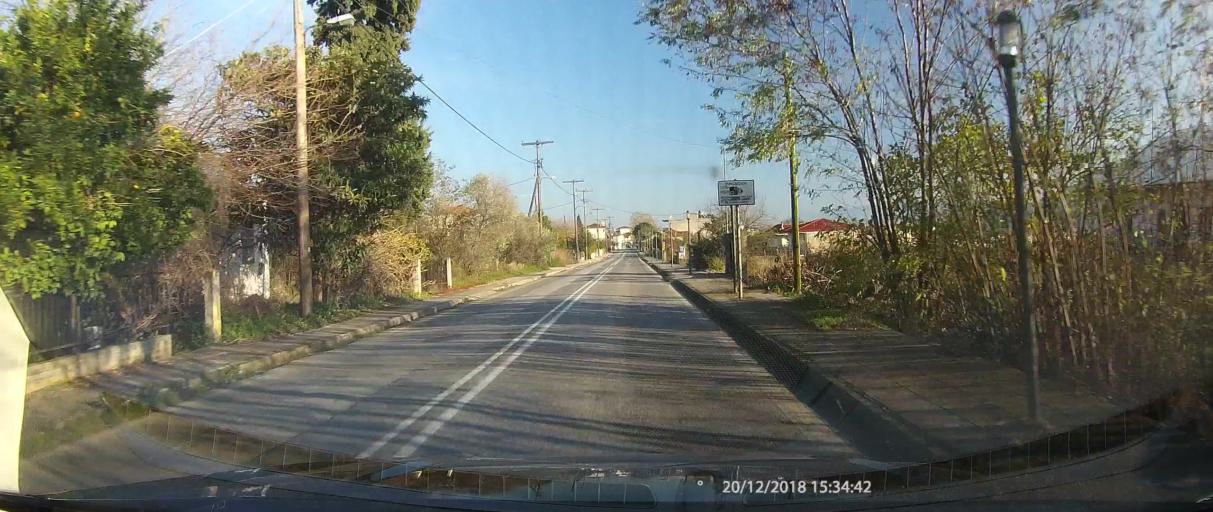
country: GR
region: Central Greece
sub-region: Nomos Fthiotidos
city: Lianokladhion
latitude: 38.9181
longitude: 22.2975
